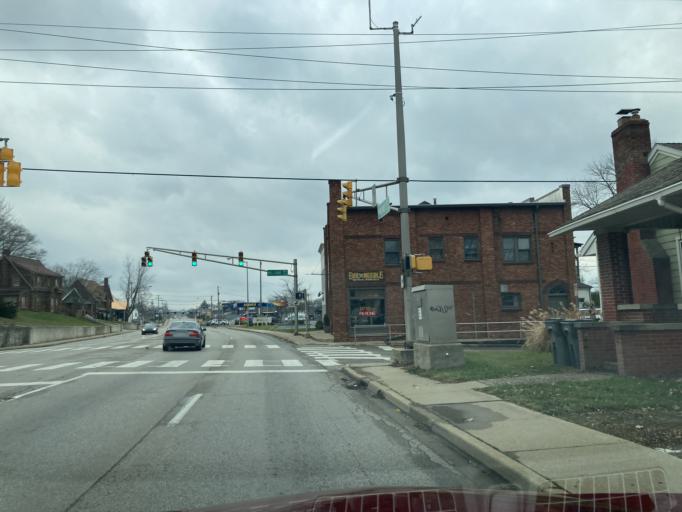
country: US
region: Indiana
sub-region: Monroe County
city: Bloomington
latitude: 39.1508
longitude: -86.5338
